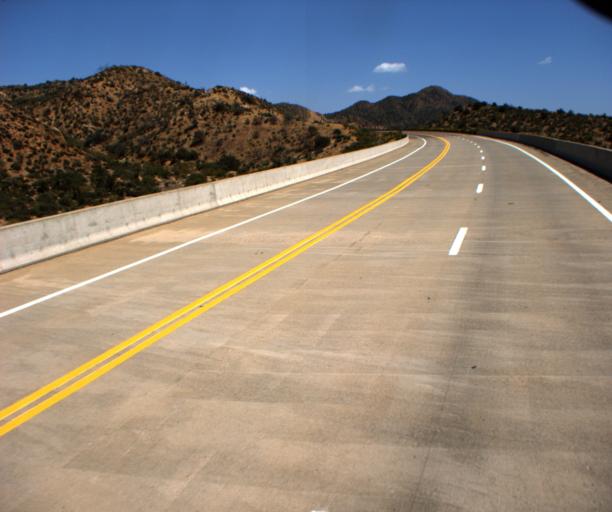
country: US
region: Arizona
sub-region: Gila County
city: Miami
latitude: 33.5510
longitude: -110.9478
